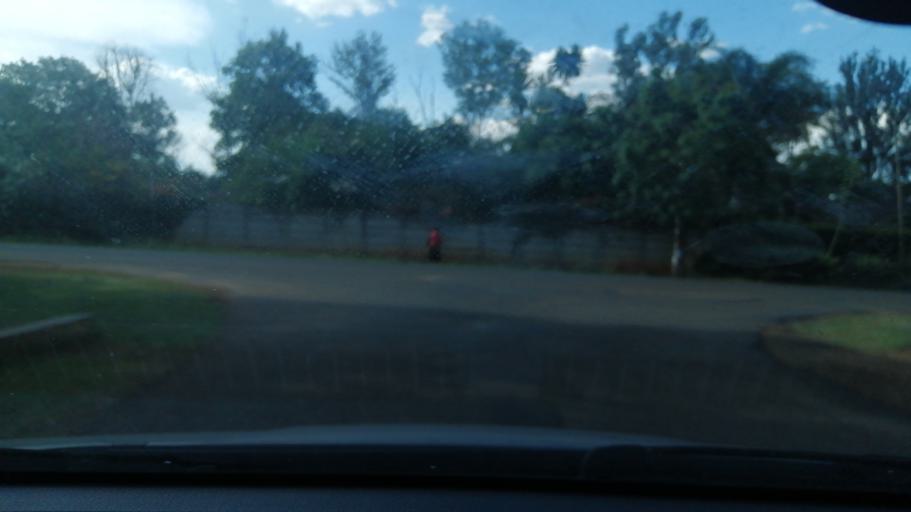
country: ZW
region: Harare
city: Harare
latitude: -17.7649
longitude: 31.0600
